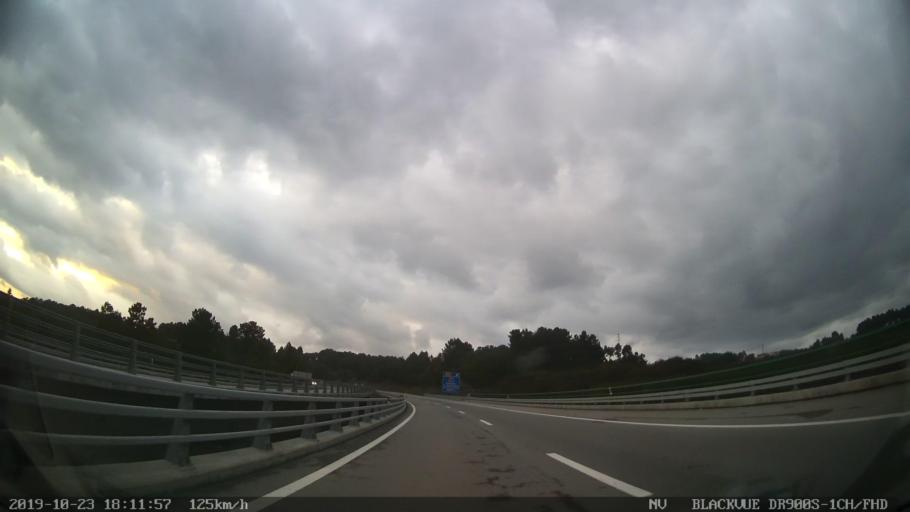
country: PT
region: Vila Real
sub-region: Vila Real
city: Vila Real
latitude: 41.3109
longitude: -7.6858
